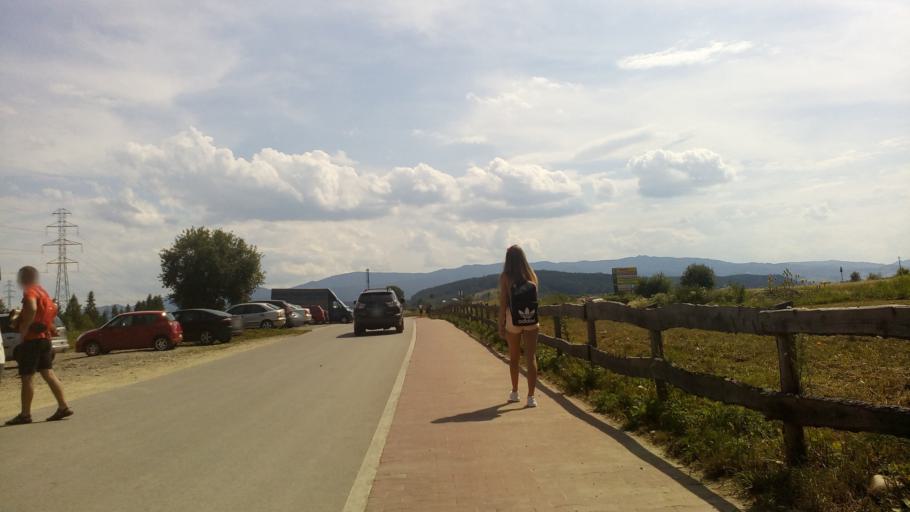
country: PL
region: Lesser Poland Voivodeship
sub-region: Powiat nowosadecki
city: Stary Sacz
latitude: 49.5827
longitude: 20.6385
